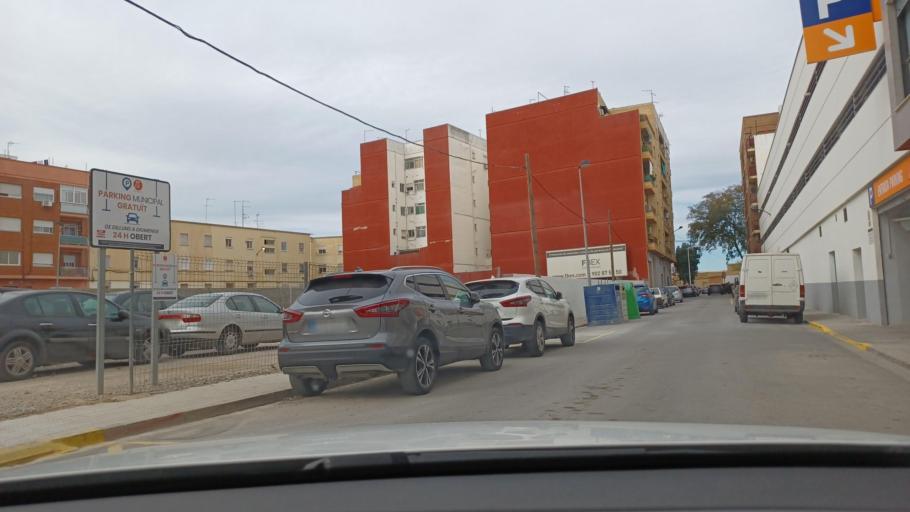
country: ES
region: Valencia
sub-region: Provincia de Valencia
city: Picassent
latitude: 39.3657
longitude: -0.4603
